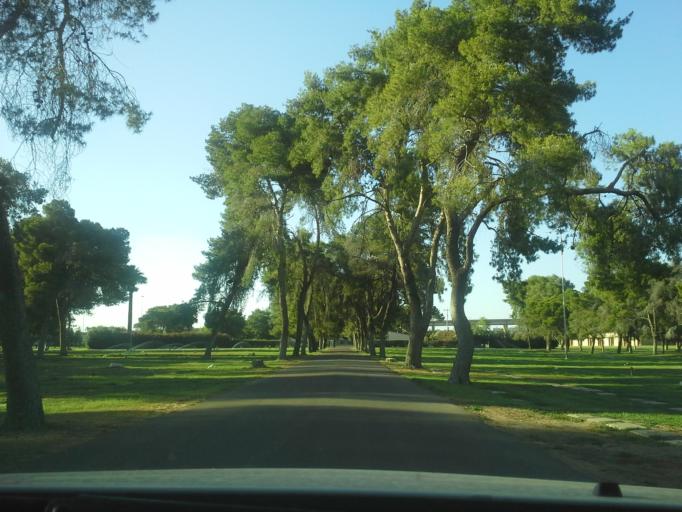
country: US
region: Arizona
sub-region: Maricopa County
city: Phoenix
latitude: 33.4570
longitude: -112.1123
